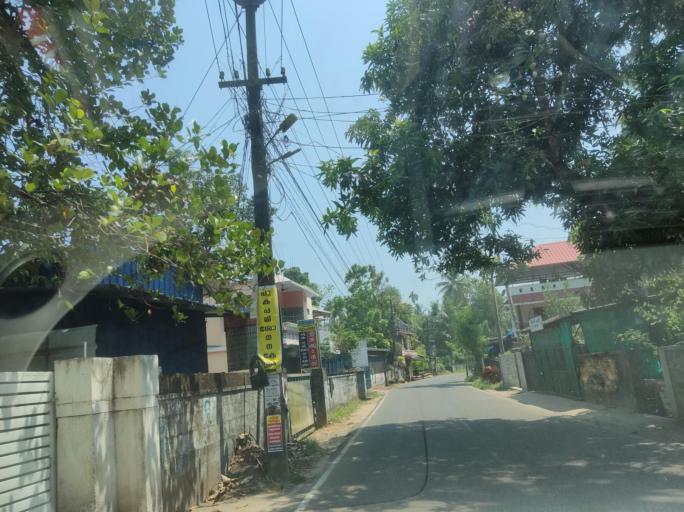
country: IN
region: Kerala
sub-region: Alappuzha
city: Kutiatodu
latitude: 9.8285
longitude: 76.2980
